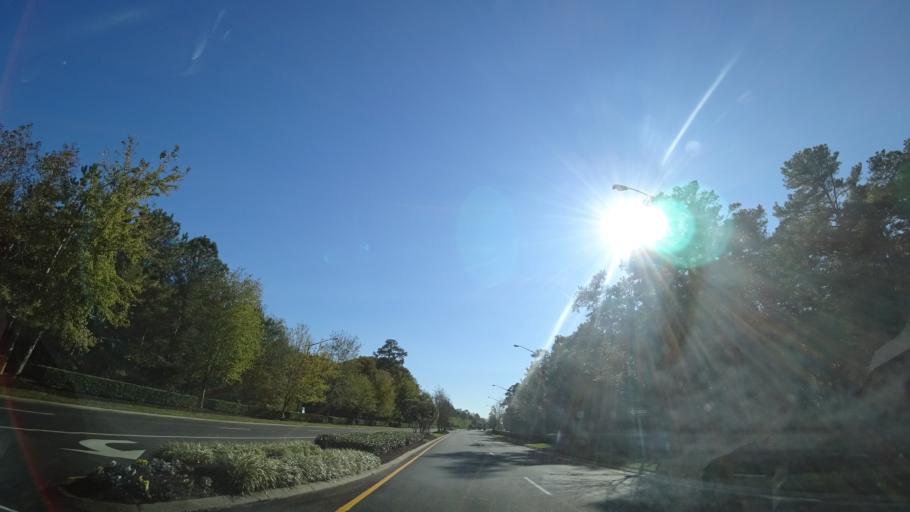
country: US
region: Virginia
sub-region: City of Portsmouth
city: Portsmouth Heights
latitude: 36.8824
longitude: -76.4371
